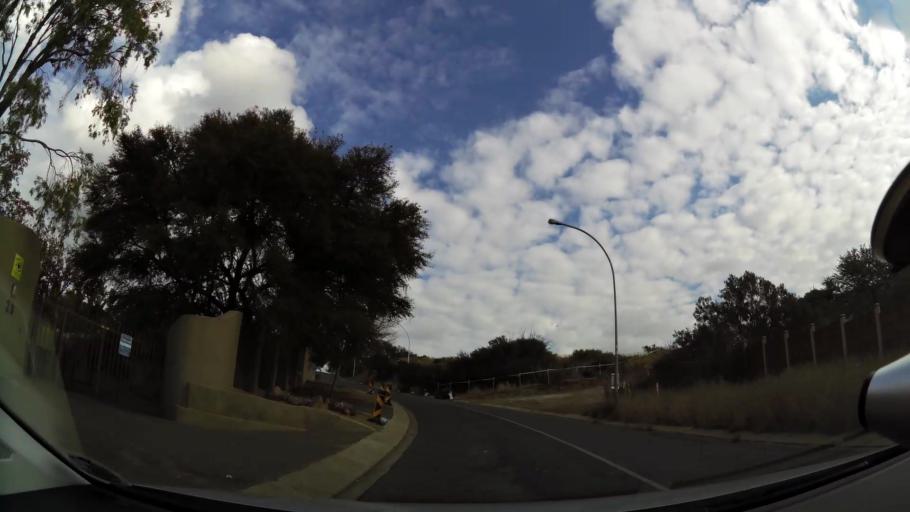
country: ZA
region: Orange Free State
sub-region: Mangaung Metropolitan Municipality
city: Bloemfontein
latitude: -29.0739
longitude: 26.2082
